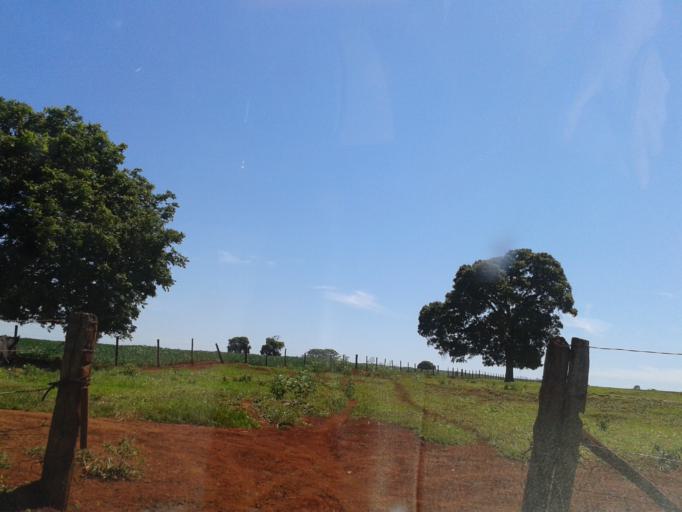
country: BR
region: Minas Gerais
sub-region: Centralina
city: Centralina
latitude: -18.6360
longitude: -49.2950
